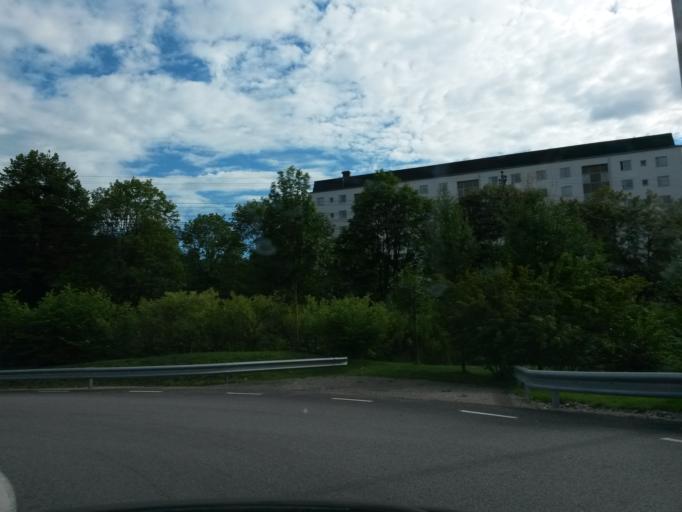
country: SE
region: Vaestra Goetaland
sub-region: Boras Kommun
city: Boras
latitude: 57.7277
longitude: 12.9310
